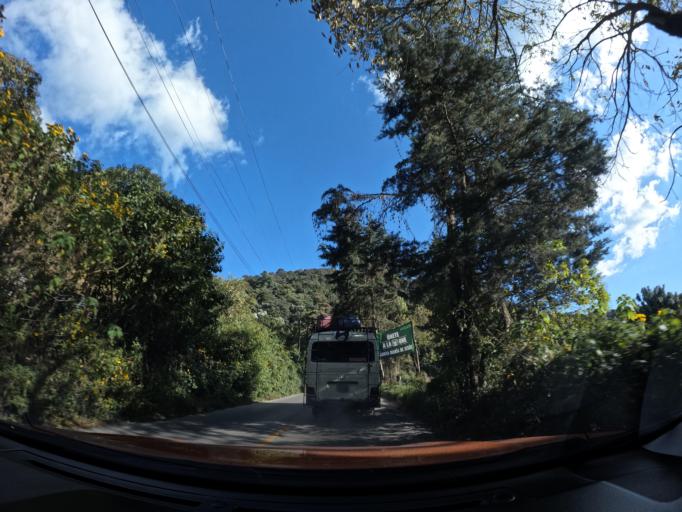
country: GT
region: Sacatepequez
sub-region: Municipio de Santa Maria de Jesus
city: Santa Maria de Jesus
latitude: 14.5023
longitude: -90.7105
